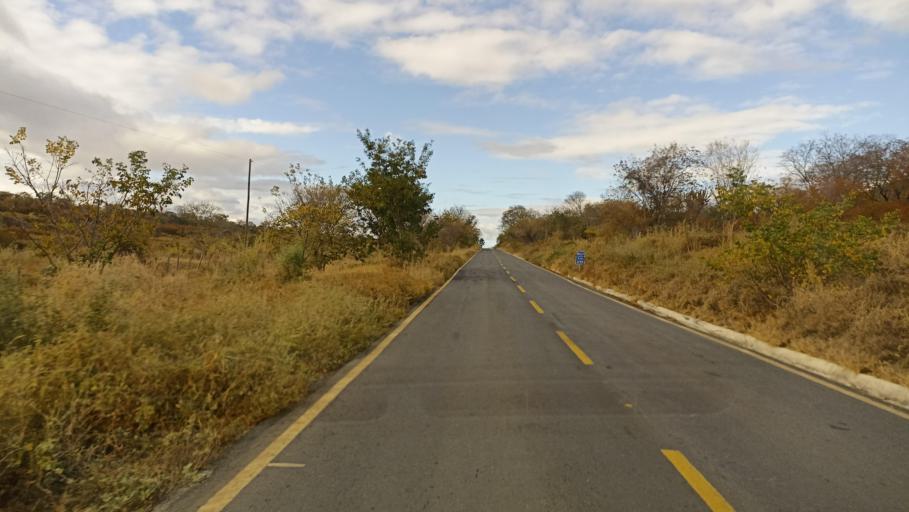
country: BR
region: Minas Gerais
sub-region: Itinga
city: Itinga
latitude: -16.5919
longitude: -41.6883
